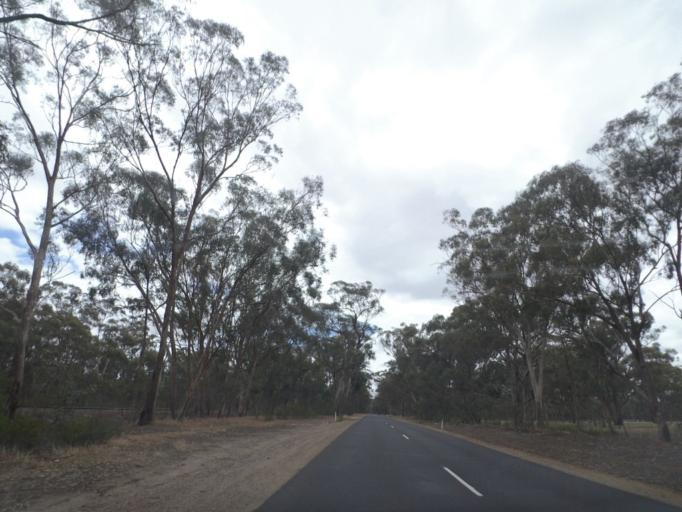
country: AU
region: Victoria
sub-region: Murrindindi
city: Kinglake West
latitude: -36.9721
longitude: 145.1643
